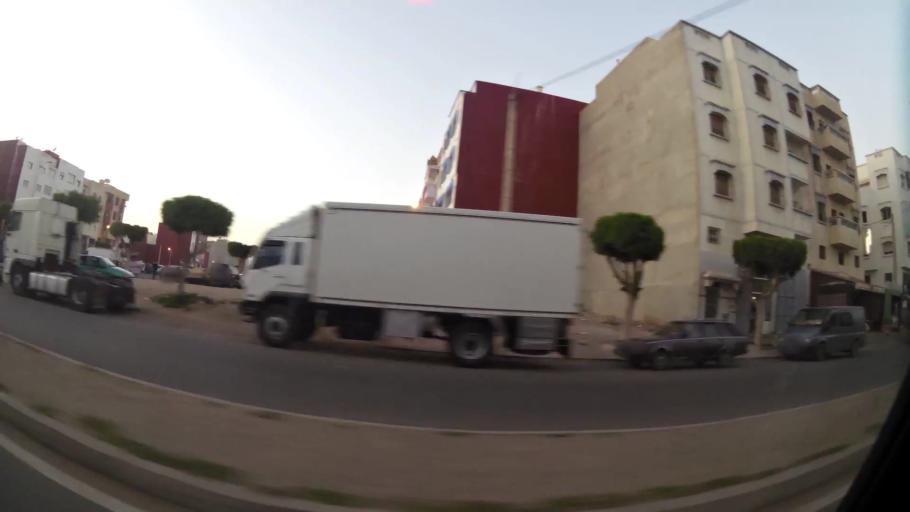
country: MA
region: Souss-Massa-Draa
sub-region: Inezgane-Ait Mellou
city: Inezgane
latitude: 30.3787
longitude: -9.5013
